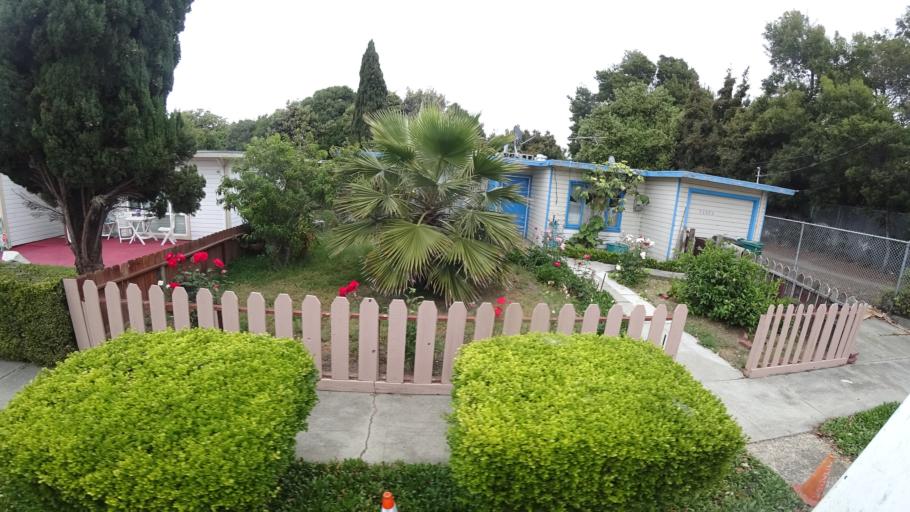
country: US
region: California
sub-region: Alameda County
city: Hayward
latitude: 37.6610
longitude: -122.0972
